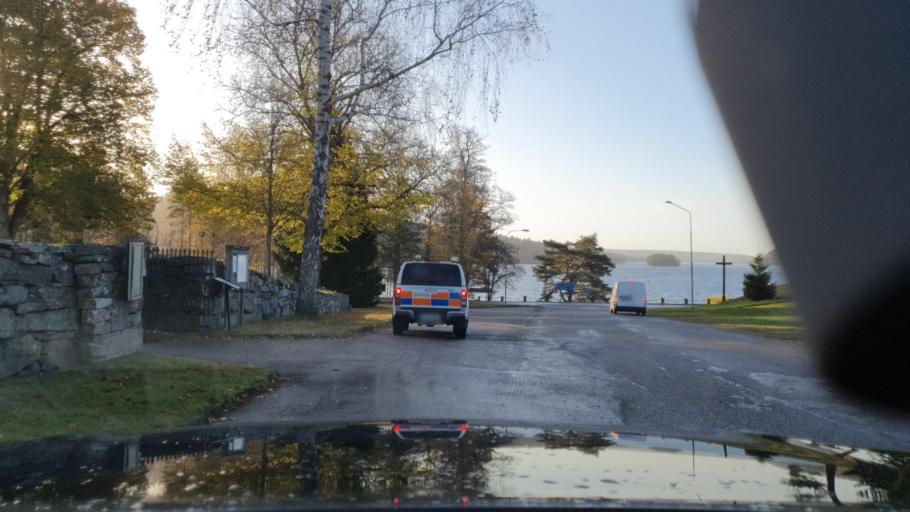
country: SE
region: Vaermland
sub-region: Grums Kommun
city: Slottsbron
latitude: 59.4552
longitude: 12.9169
